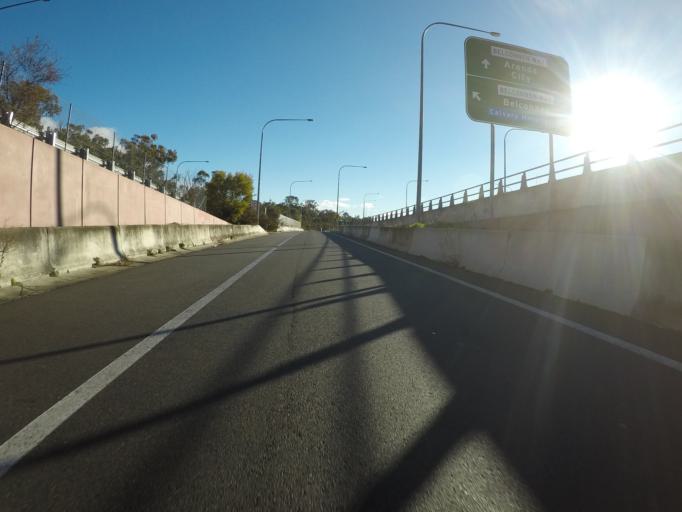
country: AU
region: Australian Capital Territory
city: Macquarie
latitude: -35.2607
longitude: 149.0868
